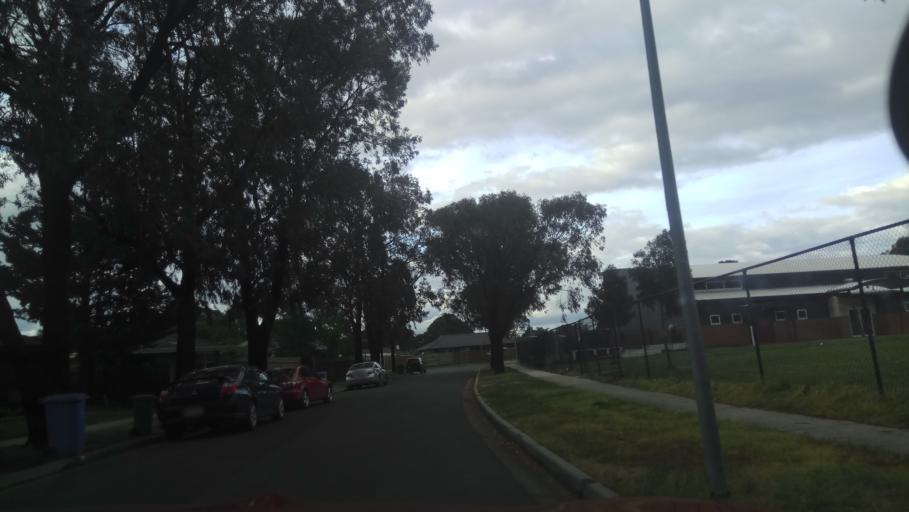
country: AU
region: Victoria
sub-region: Casey
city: Cranbourne North
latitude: -38.0773
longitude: 145.2664
